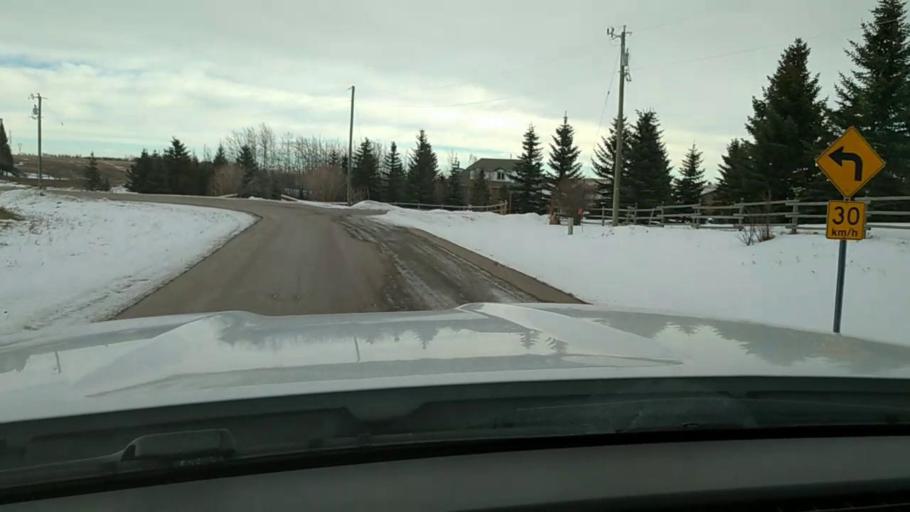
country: CA
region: Alberta
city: Cochrane
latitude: 51.2003
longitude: -114.2725
